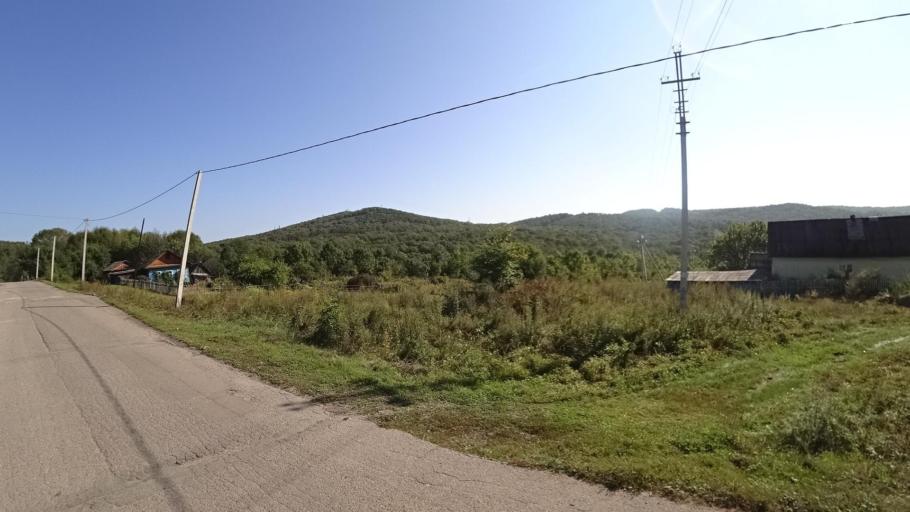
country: RU
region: Jewish Autonomous Oblast
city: Bira
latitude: 49.0112
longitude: 132.4737
